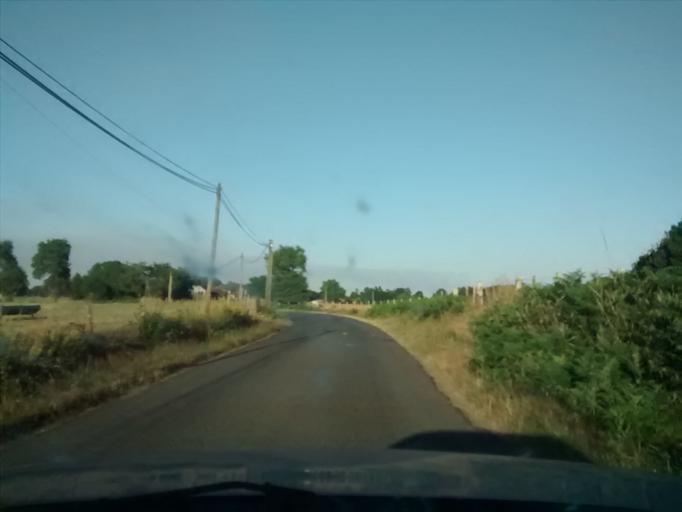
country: FR
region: Pays de la Loire
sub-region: Departement de la Sarthe
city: Loue
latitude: 48.0501
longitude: -0.1927
